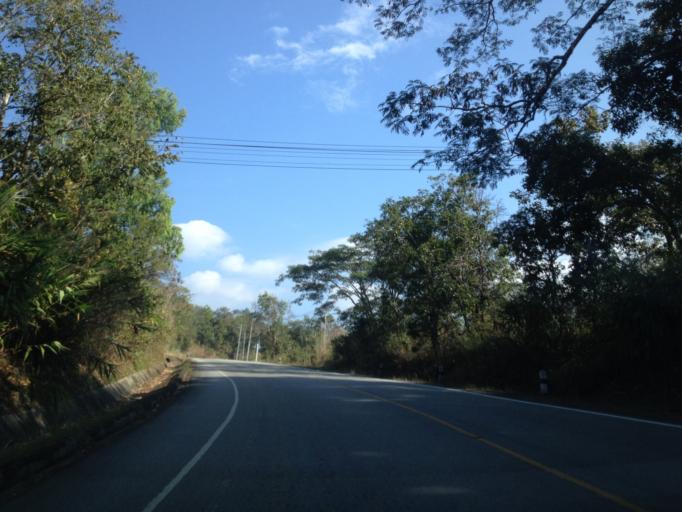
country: TH
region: Mae Hong Son
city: Pa Pae
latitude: 18.1540
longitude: 98.2740
